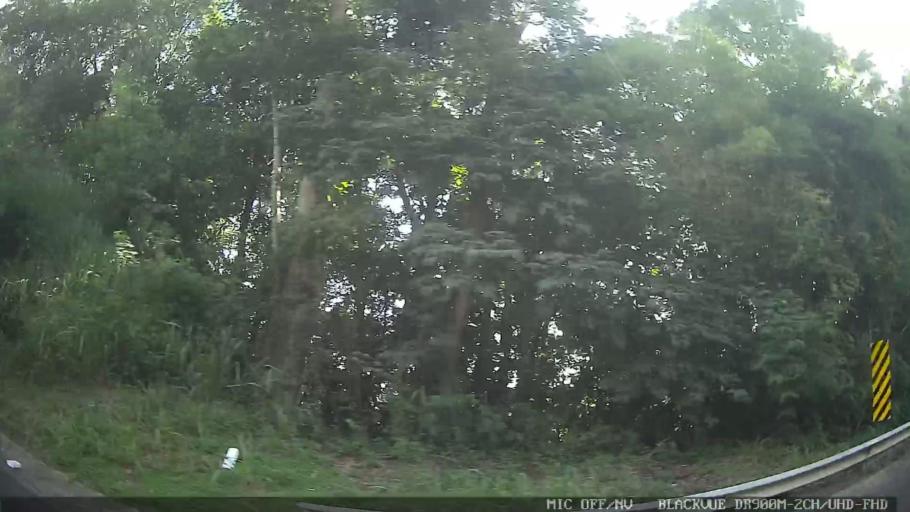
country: BR
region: Sao Paulo
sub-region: Tiete
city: Tiete
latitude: -23.1111
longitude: -47.7466
